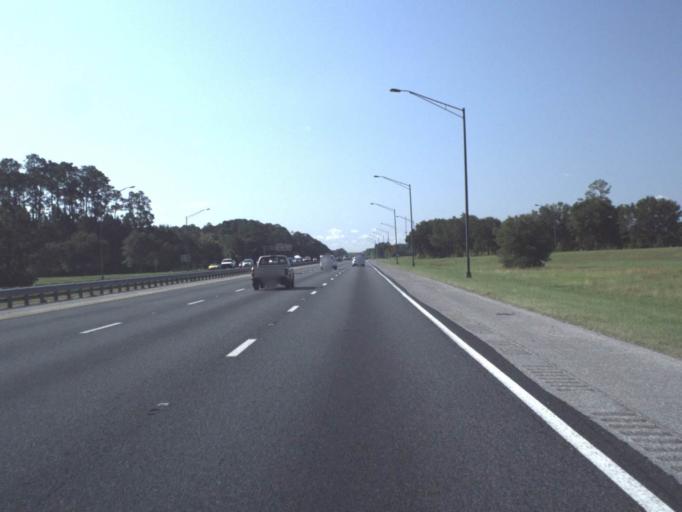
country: US
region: Florida
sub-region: Saint Johns County
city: Villano Beach
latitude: 29.9852
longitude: -81.4614
